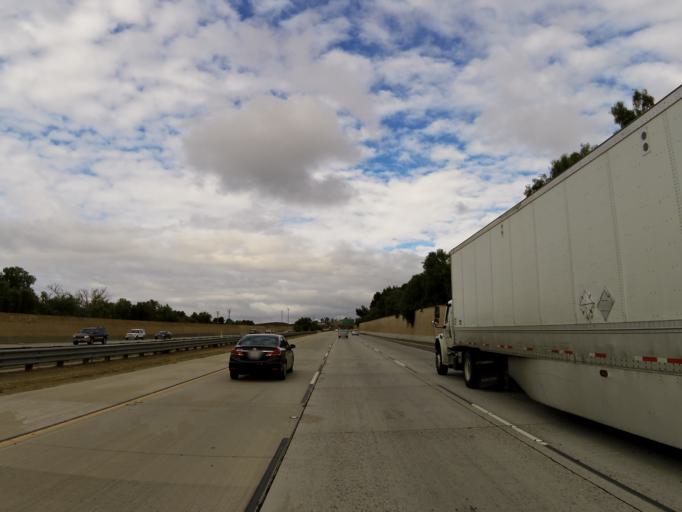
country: US
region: California
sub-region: Ventura County
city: Thousand Oaks
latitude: 34.2160
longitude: -118.8494
